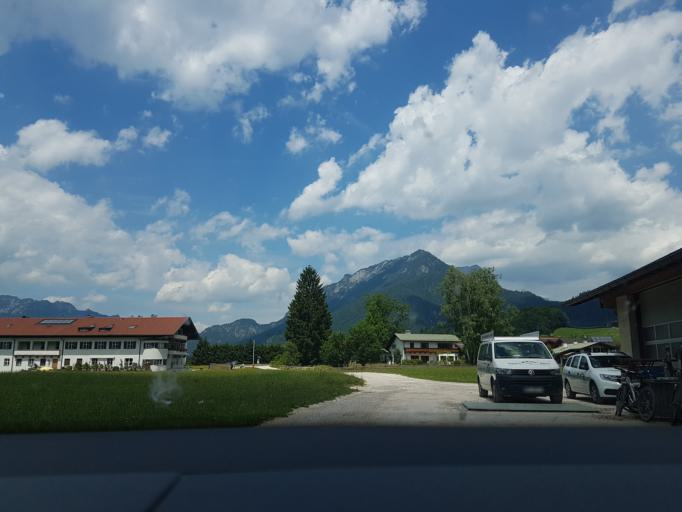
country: DE
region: Bavaria
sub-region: Upper Bavaria
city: Berchtesgaden
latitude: 47.6299
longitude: 12.9757
